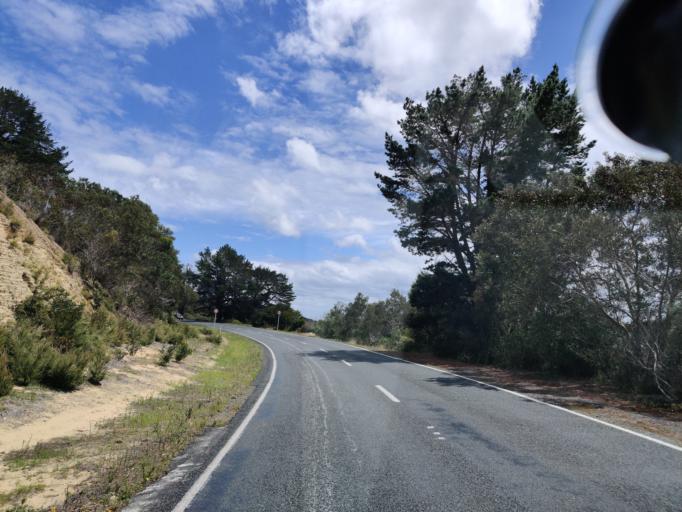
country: NZ
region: Northland
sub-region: Far North District
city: Kaitaia
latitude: -34.8051
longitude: 173.1146
